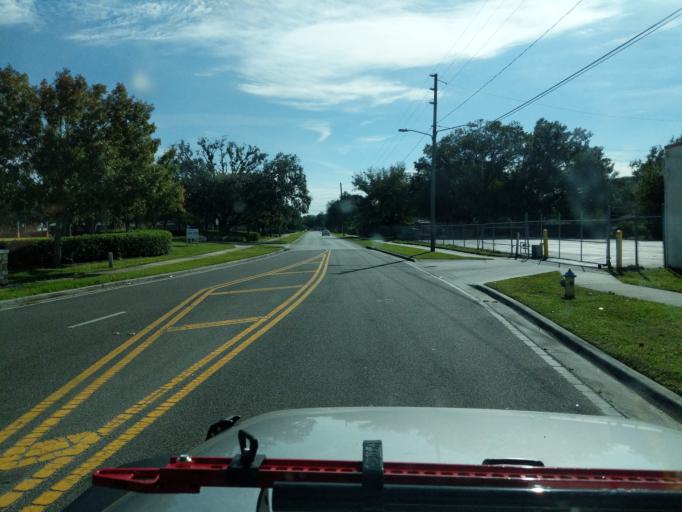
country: US
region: Florida
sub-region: Orange County
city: Winter Garden
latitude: 28.5699
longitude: -81.5670
